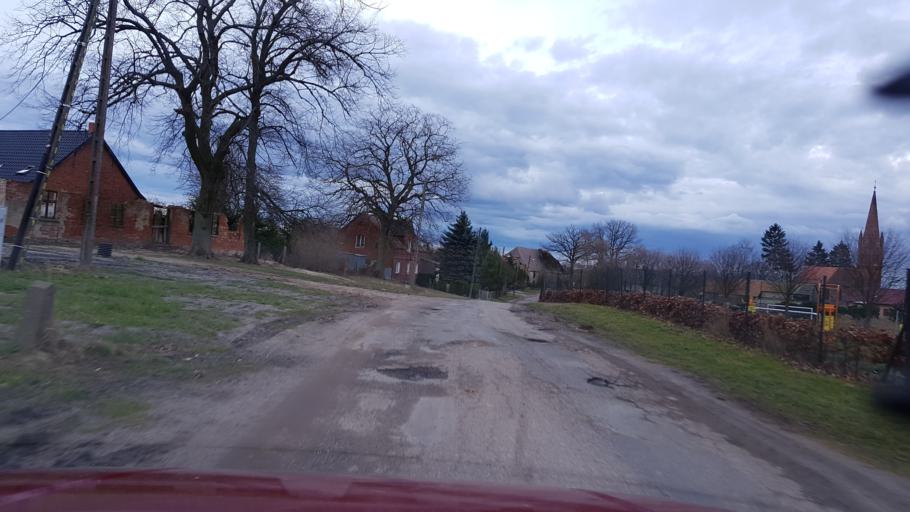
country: PL
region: West Pomeranian Voivodeship
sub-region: Powiat gryfinski
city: Stare Czarnowo
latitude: 53.3267
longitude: 14.6790
